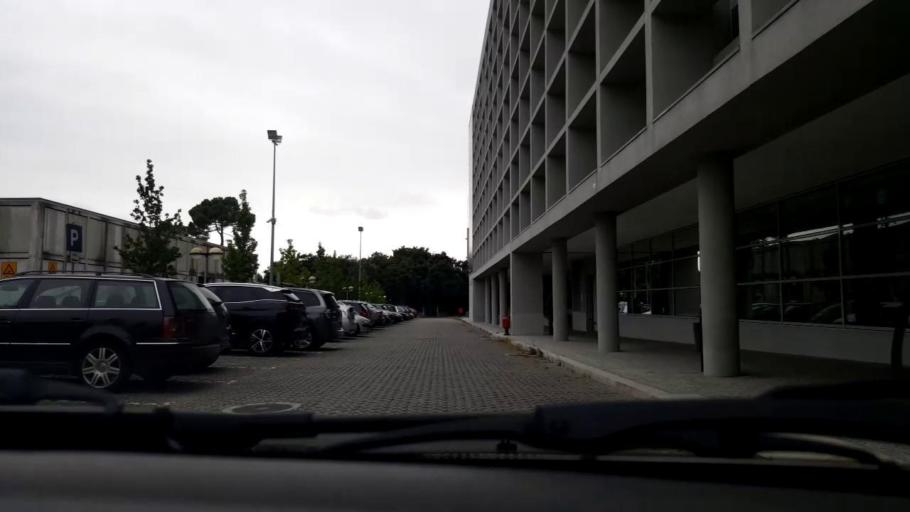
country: PT
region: Porto
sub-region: Maia
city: Pedroucos
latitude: 41.1793
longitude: -8.5948
